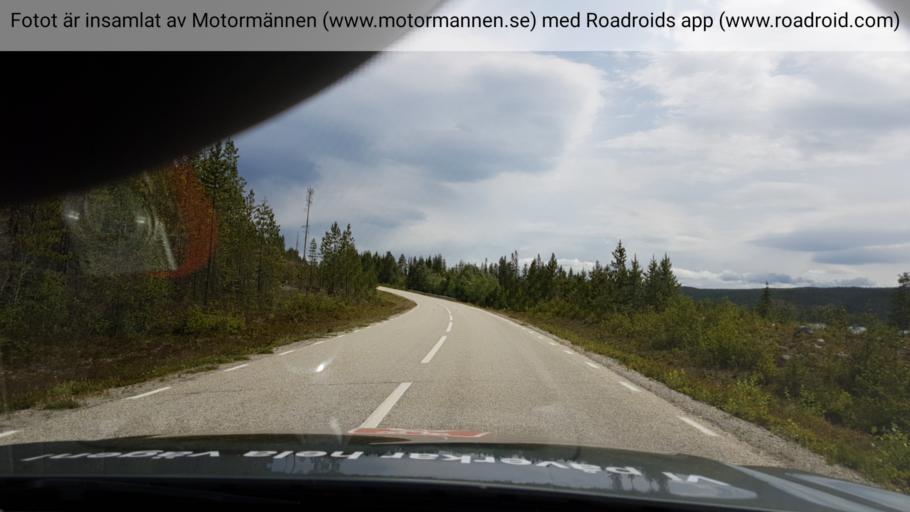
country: SE
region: Jaemtland
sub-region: Are Kommun
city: Jarpen
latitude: 62.8114
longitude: 13.5237
